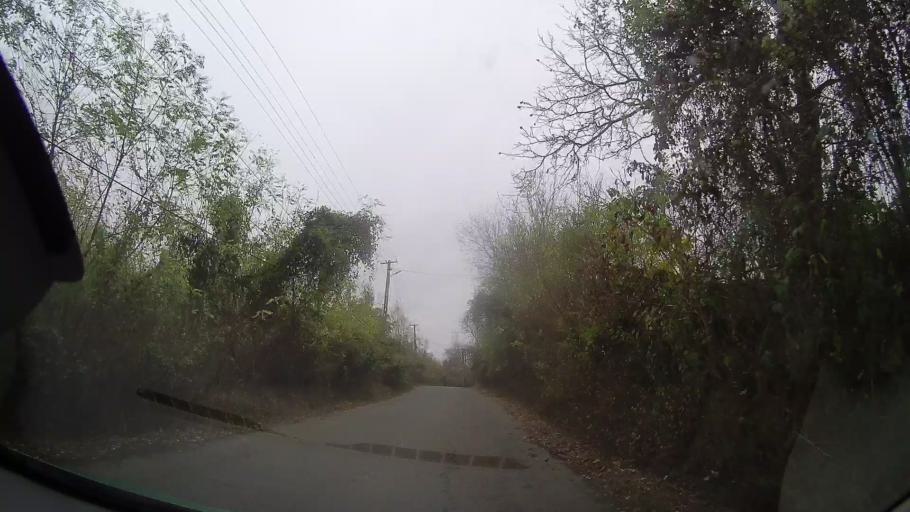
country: RO
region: Prahova
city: Mocesti
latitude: 45.0651
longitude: 26.2570
